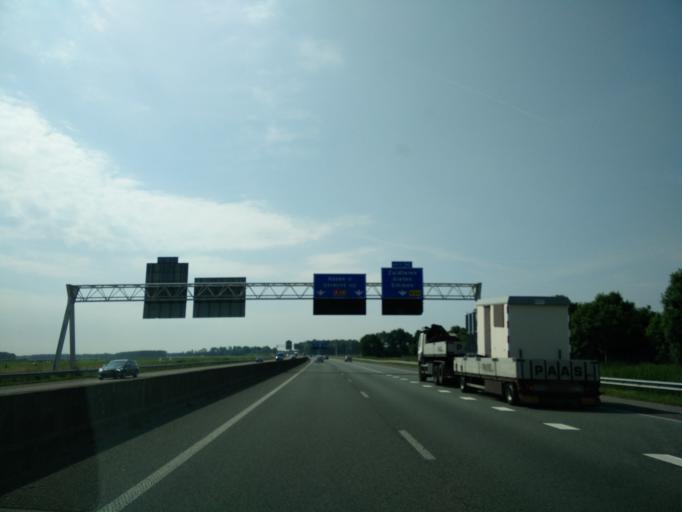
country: NL
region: Drenthe
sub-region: Gemeente Tynaarlo
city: Tynaarlo
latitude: 53.1213
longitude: 6.6104
